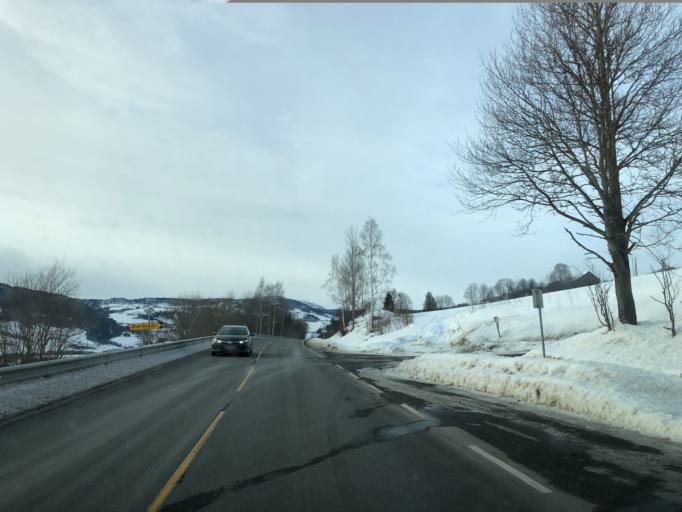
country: NO
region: Oppland
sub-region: Gausdal
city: Segalstad bru
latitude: 61.2526
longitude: 10.1827
